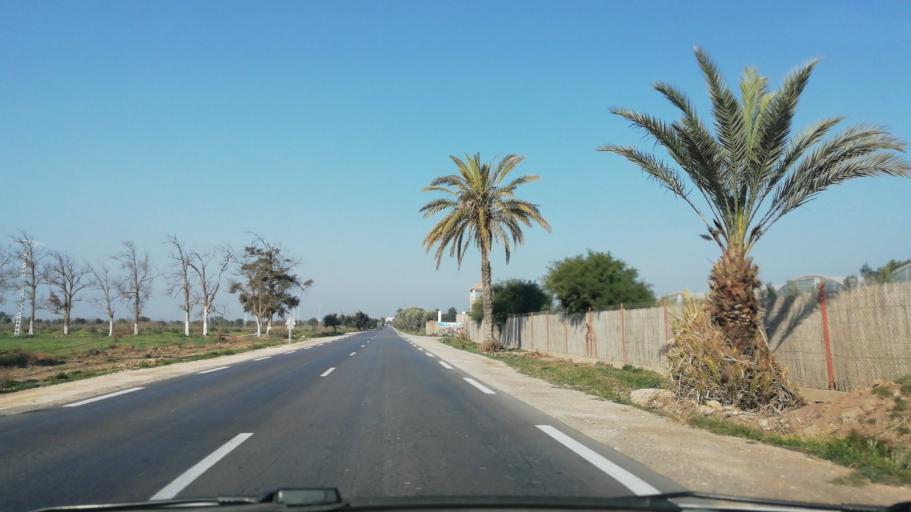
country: DZ
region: Mostaganem
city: Mostaganem
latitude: 35.7416
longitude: 0.0010
